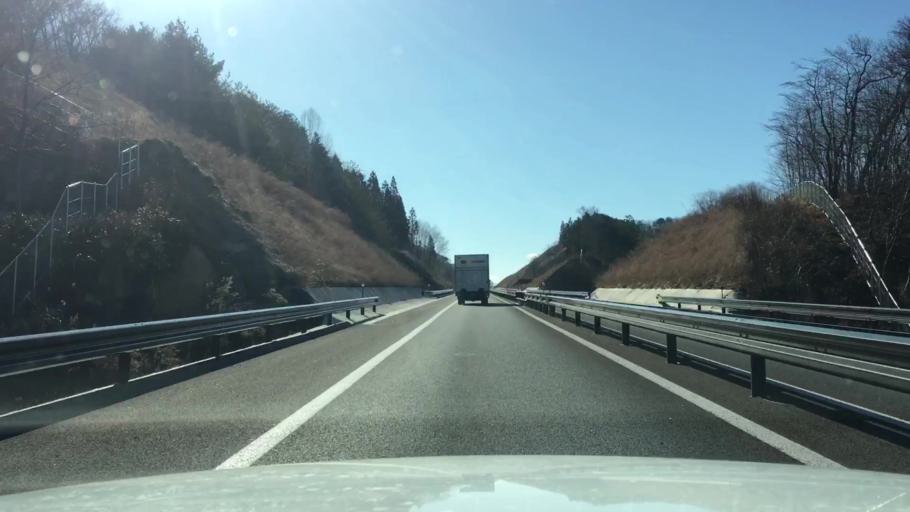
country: JP
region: Iwate
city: Miyako
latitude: 39.5582
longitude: 141.9260
